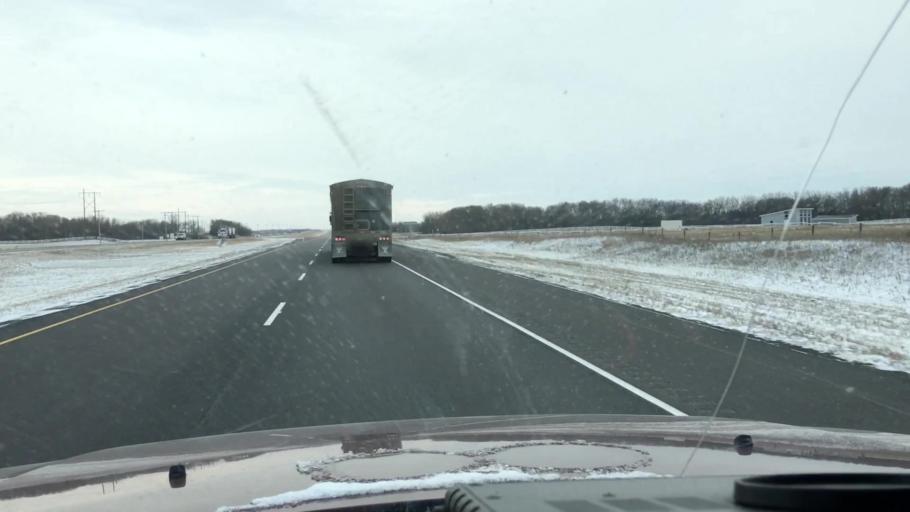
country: CA
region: Saskatchewan
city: Saskatoon
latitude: 51.9430
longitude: -106.5414
